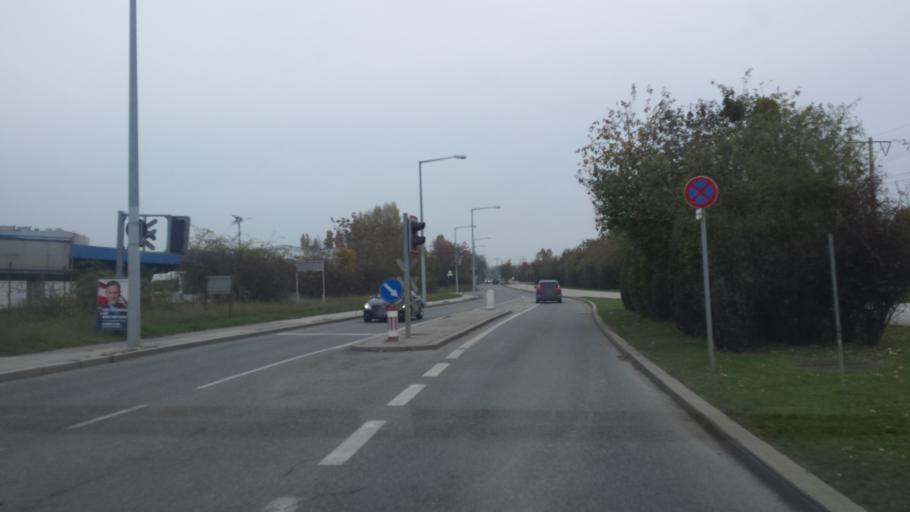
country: AT
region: Lower Austria
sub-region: Politischer Bezirk Wien-Umgebung
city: Schwechat
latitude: 48.1562
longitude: 16.4242
